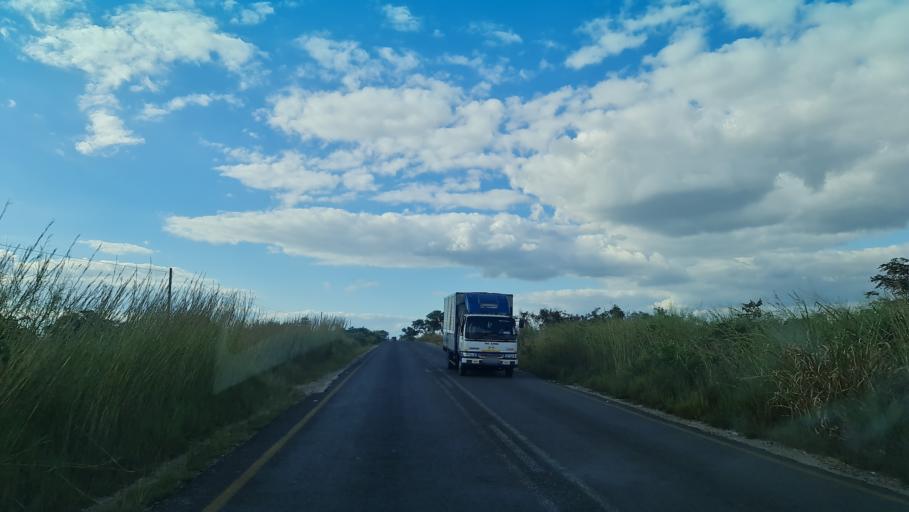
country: MZ
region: Manica
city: Chimoio
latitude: -19.2261
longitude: 33.9195
